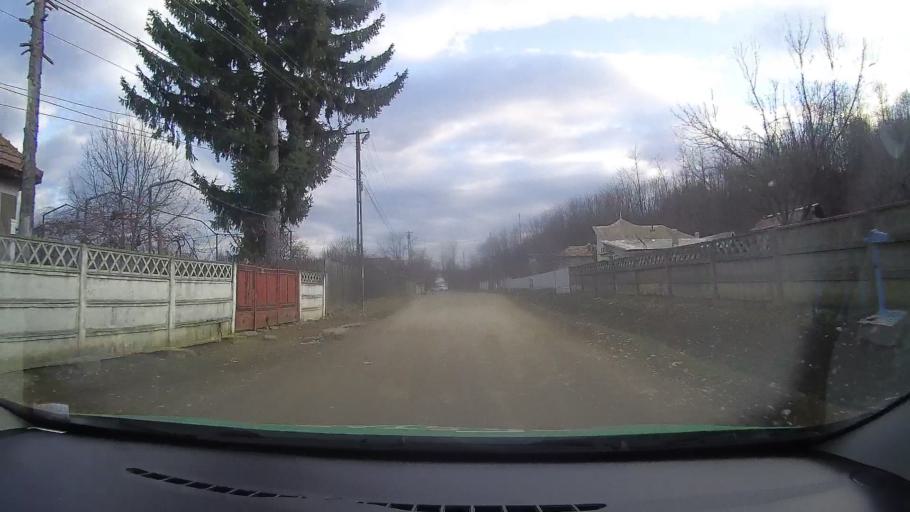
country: RO
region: Dambovita
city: Ion Luca Caragiale
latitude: 44.9121
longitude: 25.6934
